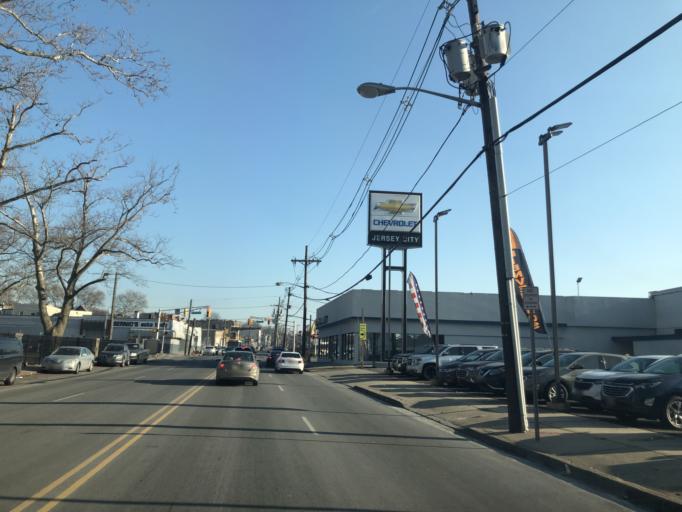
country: US
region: New Jersey
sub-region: Hudson County
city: Jersey City
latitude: 40.7228
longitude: -74.0866
